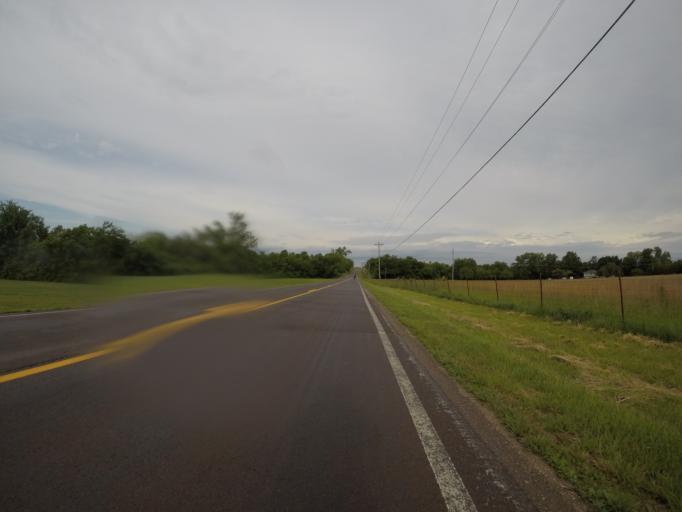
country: US
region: Kansas
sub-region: Shawnee County
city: Auburn
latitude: 38.9562
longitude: -95.7946
